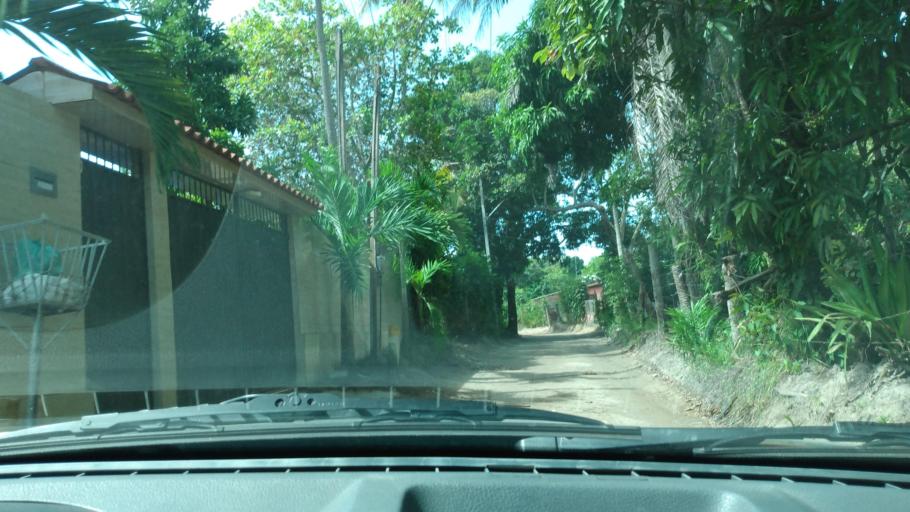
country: BR
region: Pernambuco
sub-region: Cabo De Santo Agostinho
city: Cabo
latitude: -8.3537
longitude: -34.9652
